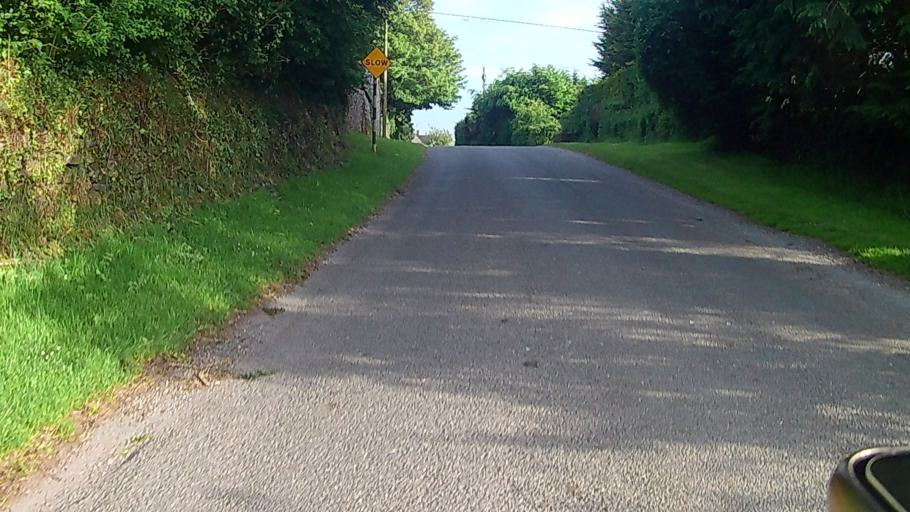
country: IE
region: Munster
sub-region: County Cork
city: Cork
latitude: 51.9852
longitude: -8.4581
